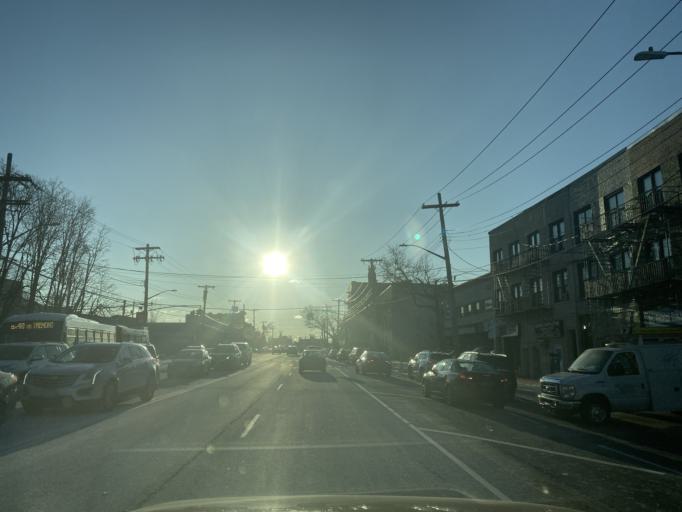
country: US
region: New York
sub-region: Bronx
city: The Bronx
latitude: 40.8395
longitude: -73.8368
